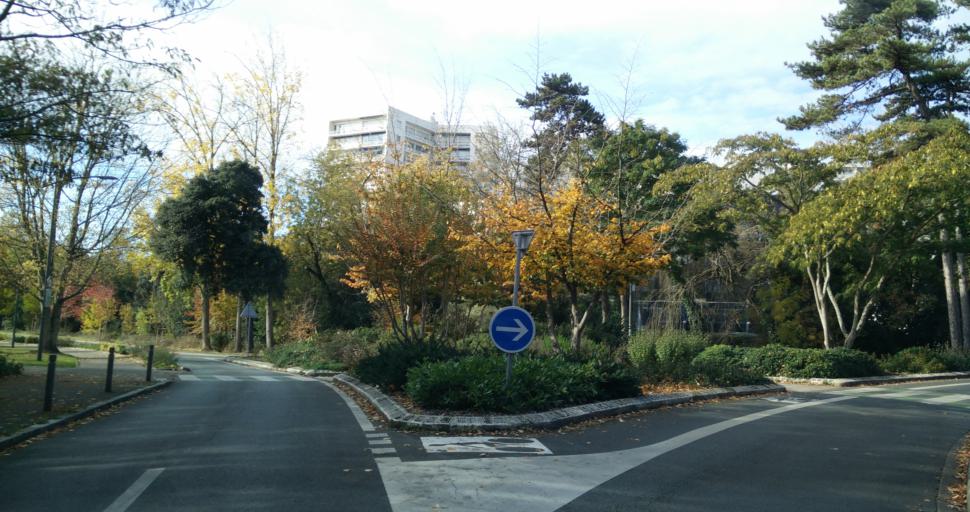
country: FR
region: Poitou-Charentes
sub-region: Departement de la Charente-Maritime
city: La Rochelle
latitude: 46.1604
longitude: -1.1575
